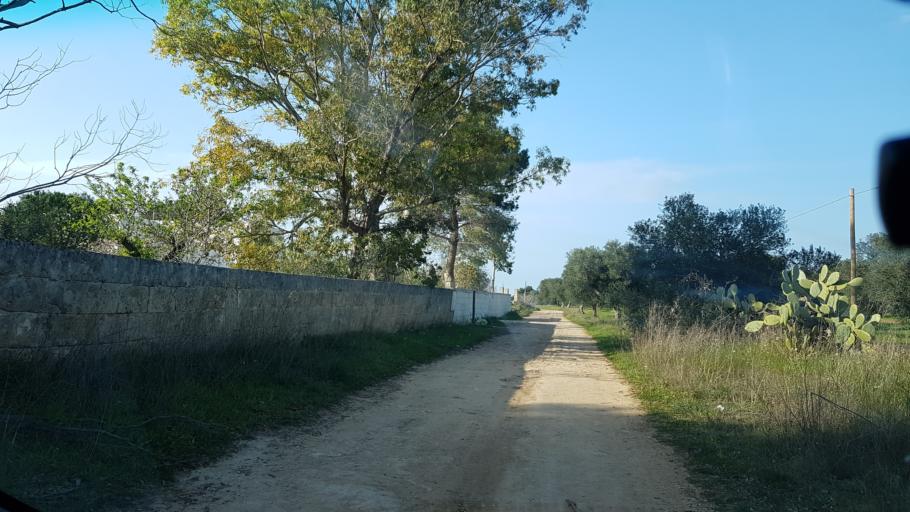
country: IT
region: Apulia
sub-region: Provincia di Brindisi
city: San Vito dei Normanni
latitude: 40.6700
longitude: 17.7913
